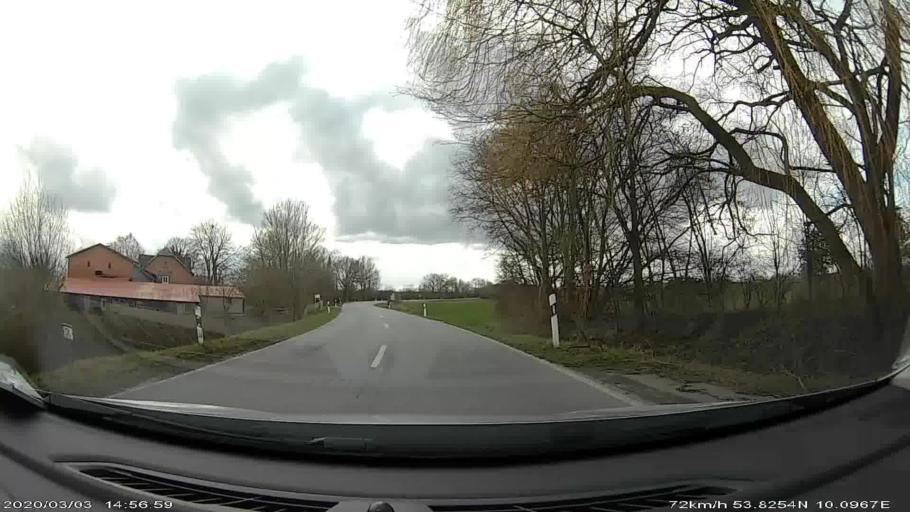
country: DE
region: Schleswig-Holstein
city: Sievershutten
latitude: 53.8256
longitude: 10.0971
